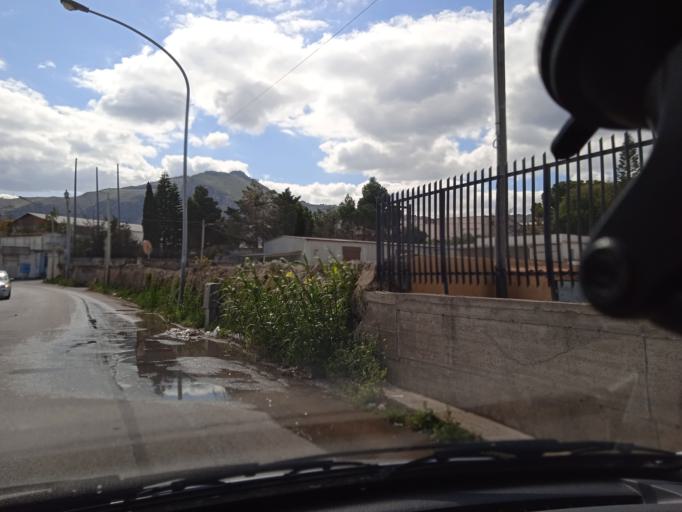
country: IT
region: Sicily
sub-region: Palermo
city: Villabate
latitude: 38.0844
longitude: 13.4253
